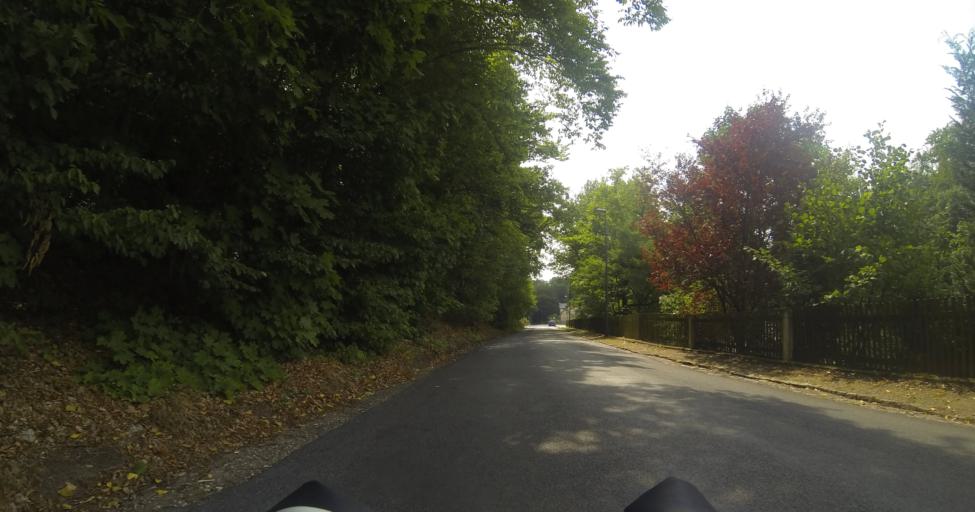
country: DE
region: Saxony
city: Radebeul
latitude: 51.1171
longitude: 13.6556
